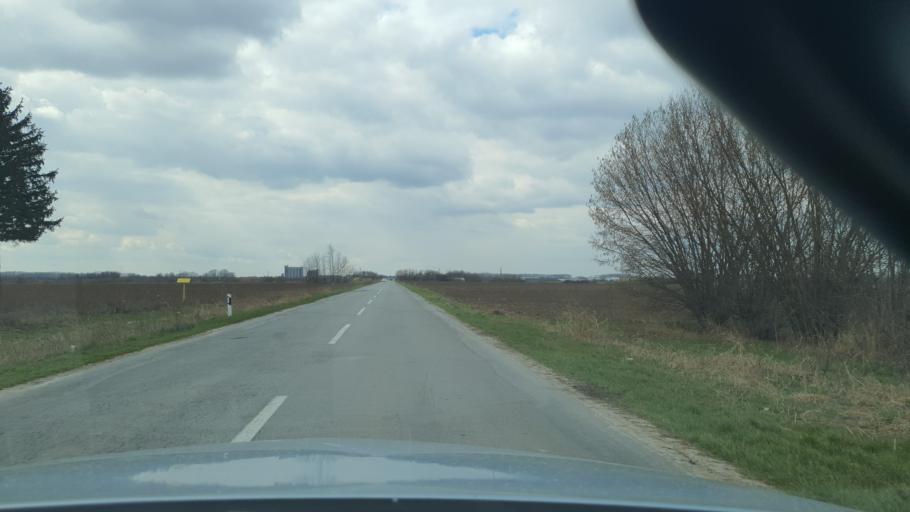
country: RS
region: Autonomna Pokrajina Vojvodina
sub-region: Juznobacki Okrug
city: Bac
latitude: 45.3987
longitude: 19.2700
